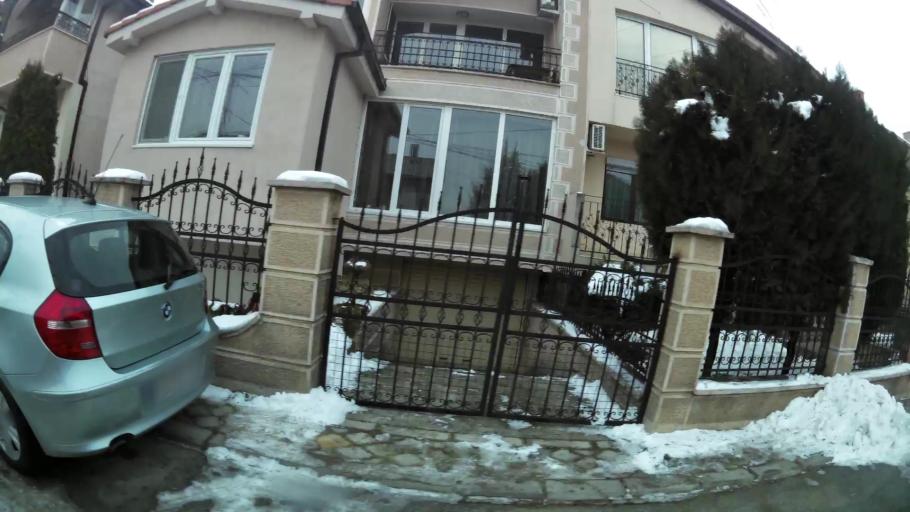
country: MK
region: Saraj
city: Saraj
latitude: 42.0227
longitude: 21.3550
